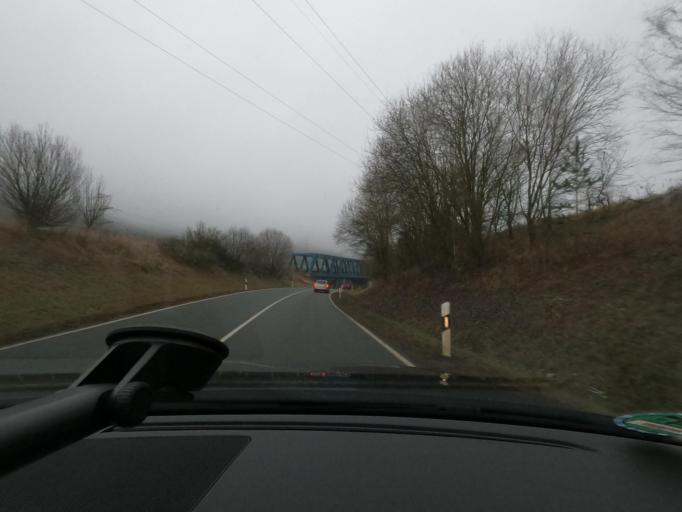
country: DE
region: Thuringia
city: Behringen
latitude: 50.7668
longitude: 11.0018
